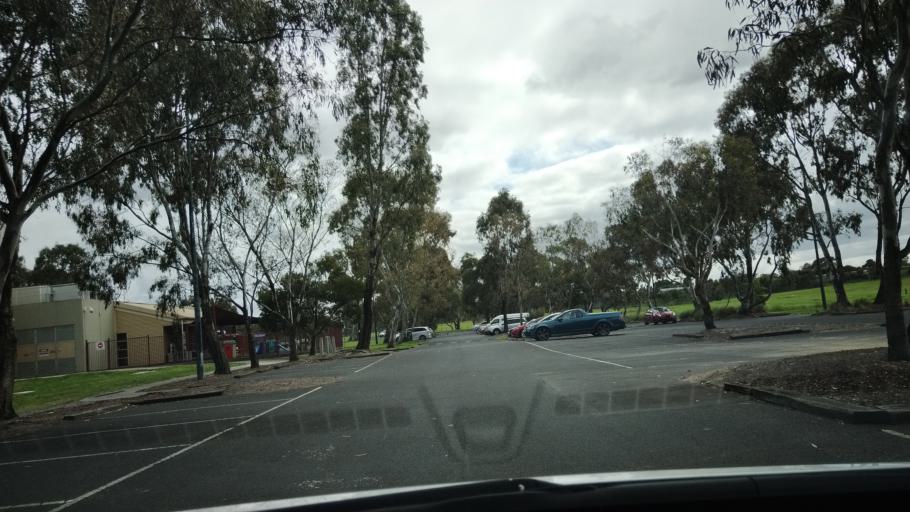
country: AU
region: Victoria
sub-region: Greater Dandenong
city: Keysborough
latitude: -37.9965
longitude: 145.1550
